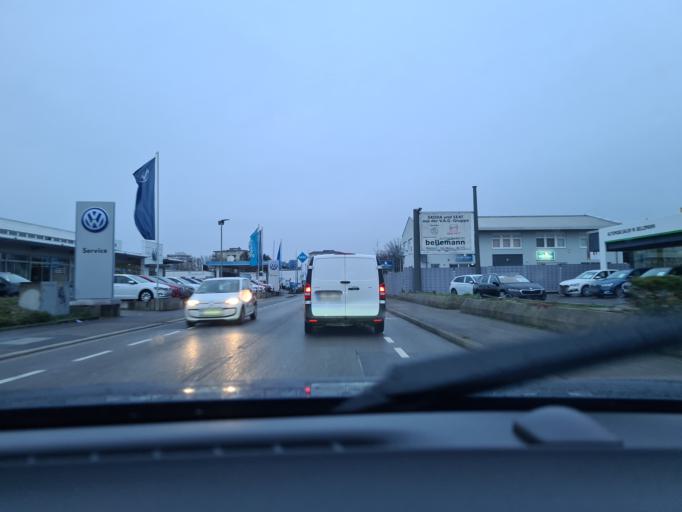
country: DE
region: Baden-Wuerttemberg
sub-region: Karlsruhe Region
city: Wiesloch
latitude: 49.2890
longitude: 8.6787
